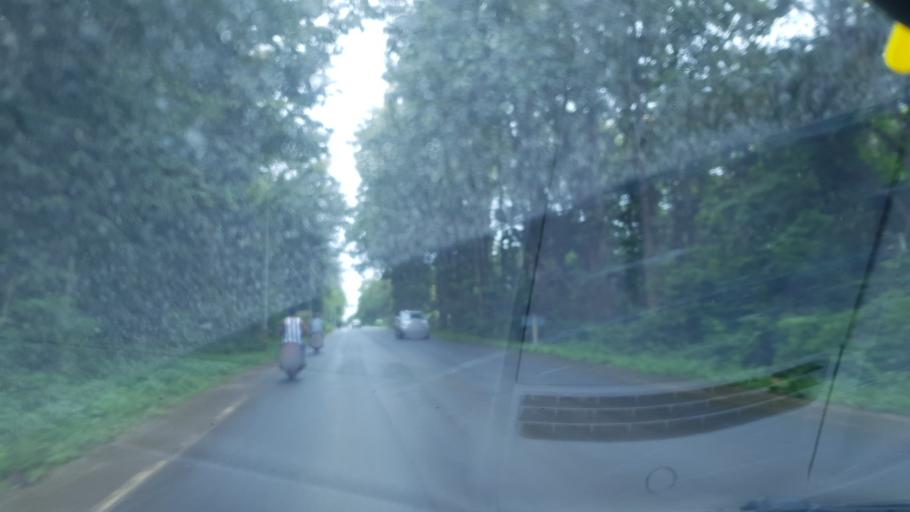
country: TH
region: Mae Hong Son
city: Pa Pae
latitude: 18.1813
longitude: 97.9347
